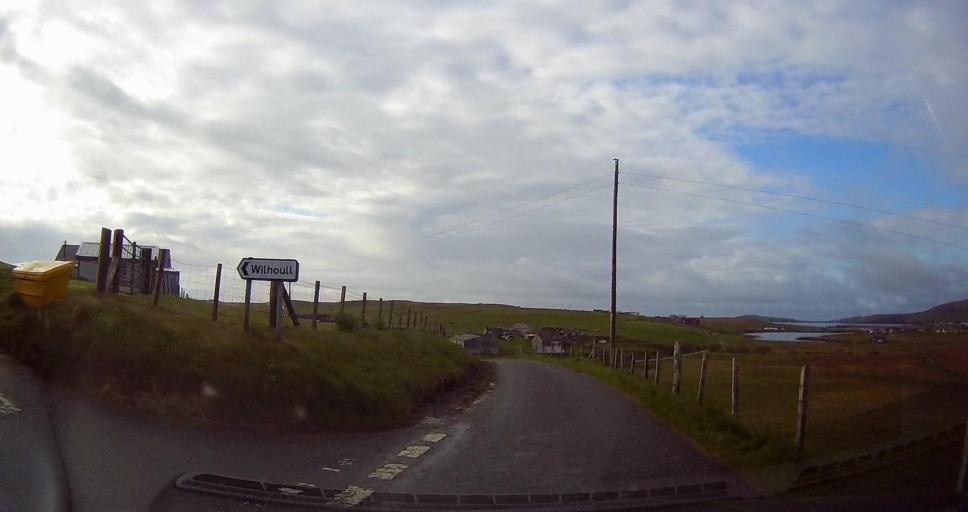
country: GB
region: Scotland
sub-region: Shetland Islands
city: Sandwick
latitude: 60.0517
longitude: -1.2076
